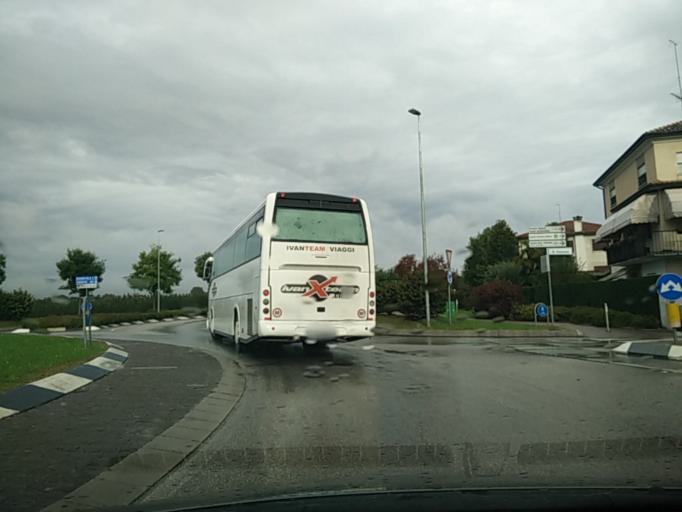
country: IT
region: Veneto
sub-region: Provincia di Vicenza
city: Rossano Veneto
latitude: 45.7090
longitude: 11.8000
